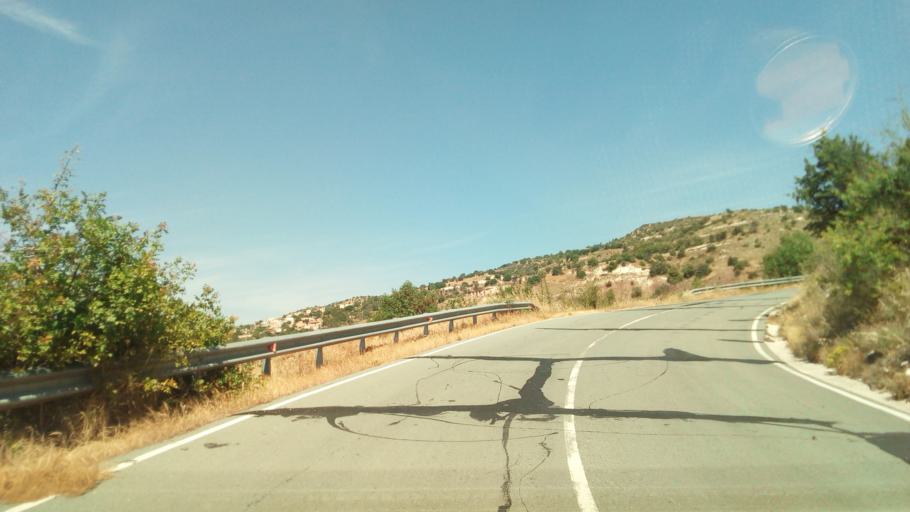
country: CY
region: Limassol
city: Pachna
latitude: 34.8002
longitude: 32.6875
